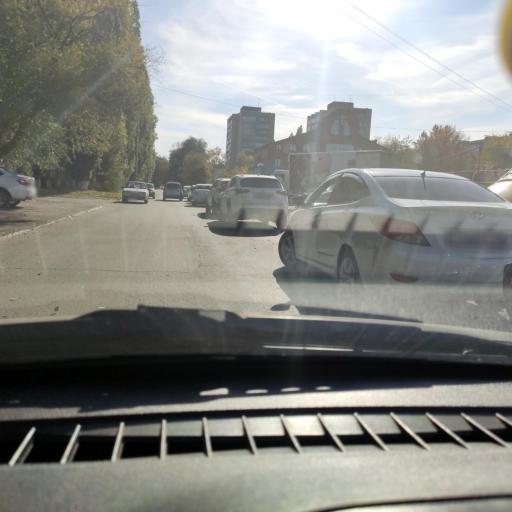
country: RU
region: Samara
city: Tol'yatti
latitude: 53.5291
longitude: 49.2660
